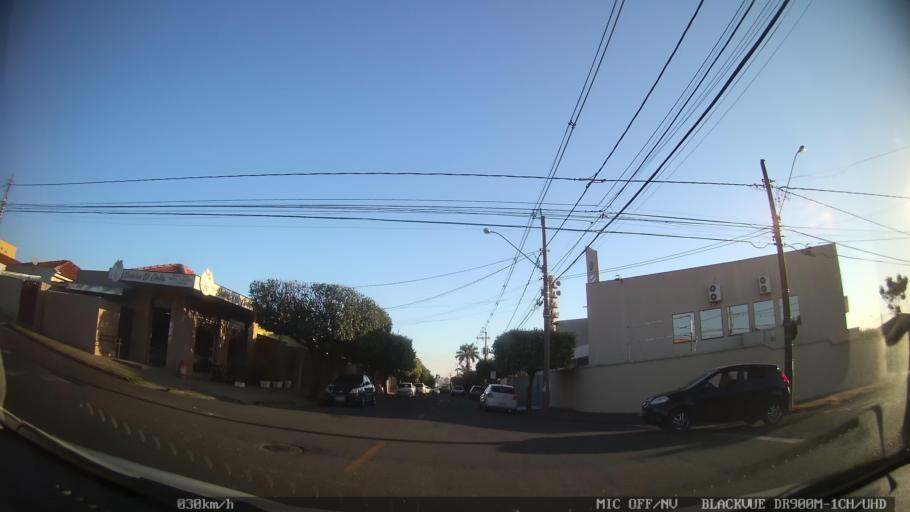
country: BR
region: Sao Paulo
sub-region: Sao Jose Do Rio Preto
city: Sao Jose do Rio Preto
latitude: -20.7945
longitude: -49.3665
